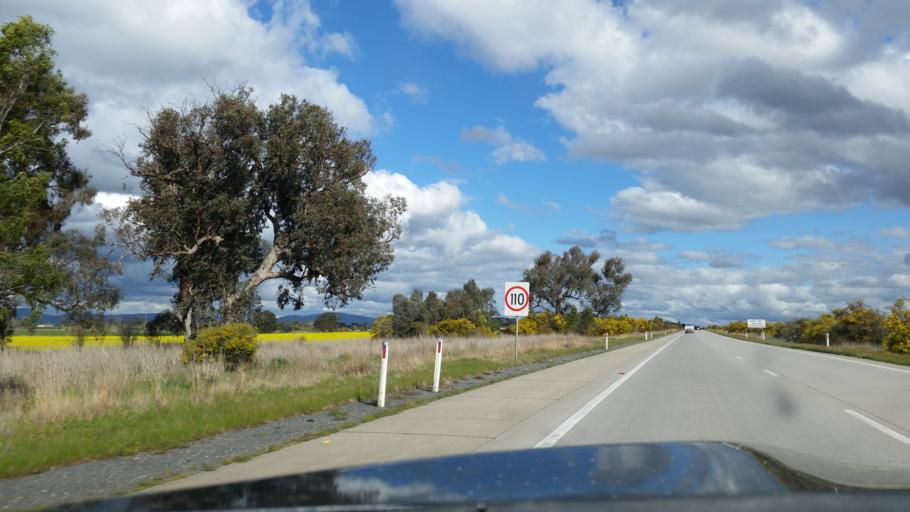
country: AU
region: New South Wales
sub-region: Greater Hume Shire
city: Jindera
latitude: -35.9512
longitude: 147.0042
